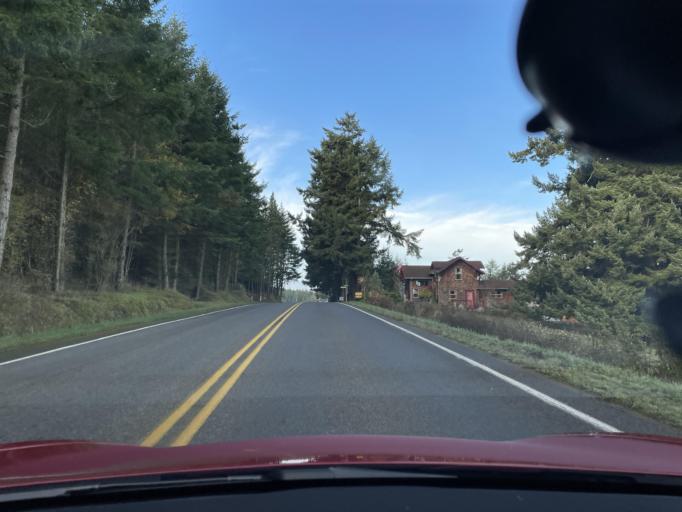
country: US
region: Washington
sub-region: San Juan County
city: Friday Harbor
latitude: 48.5399
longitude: -123.0375
